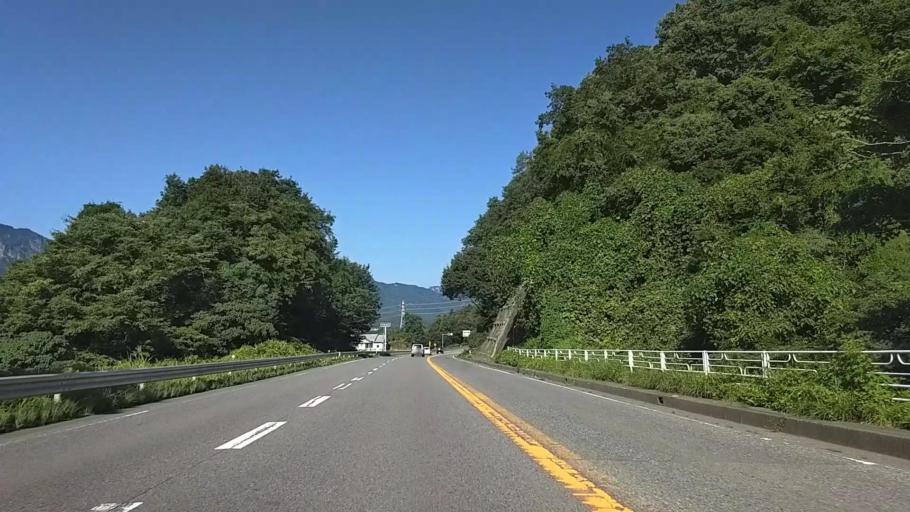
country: JP
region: Gunma
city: Annaka
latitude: 36.3172
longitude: 138.7998
